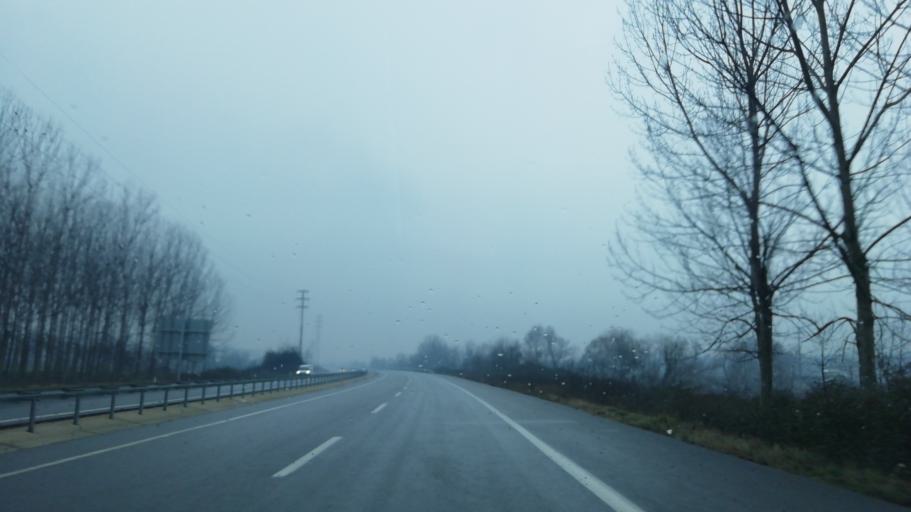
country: TR
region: Sakarya
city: Akyazi
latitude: 40.6564
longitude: 30.5983
